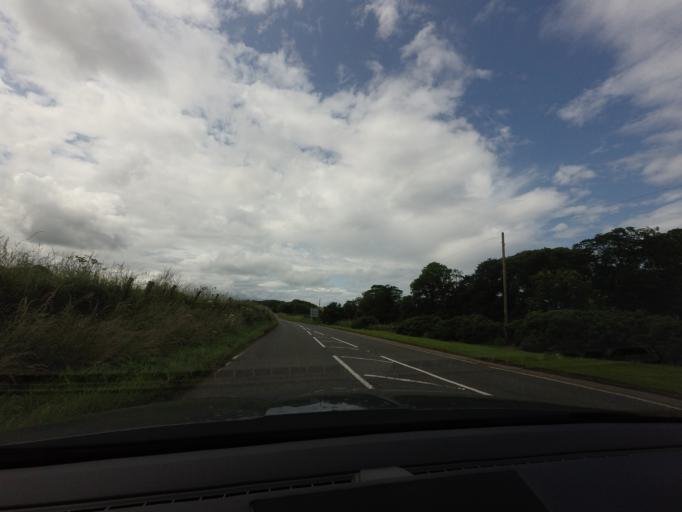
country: GB
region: Scotland
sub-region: Aberdeenshire
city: Whitehills
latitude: 57.6646
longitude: -2.5647
